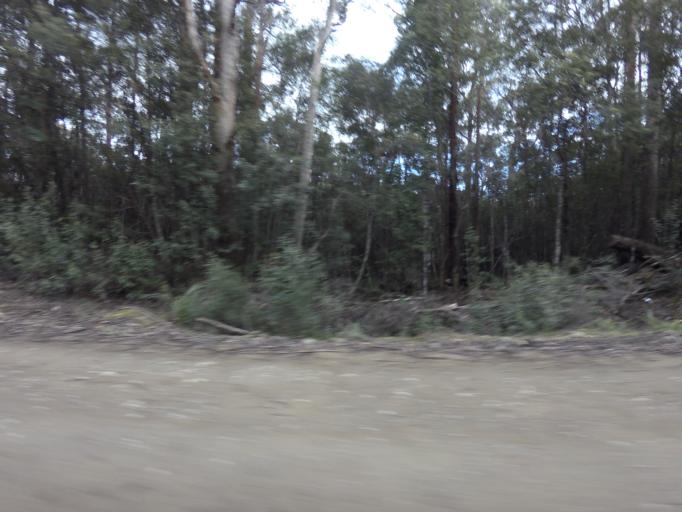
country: AU
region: Tasmania
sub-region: Huon Valley
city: Geeveston
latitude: -43.5017
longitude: 146.8780
